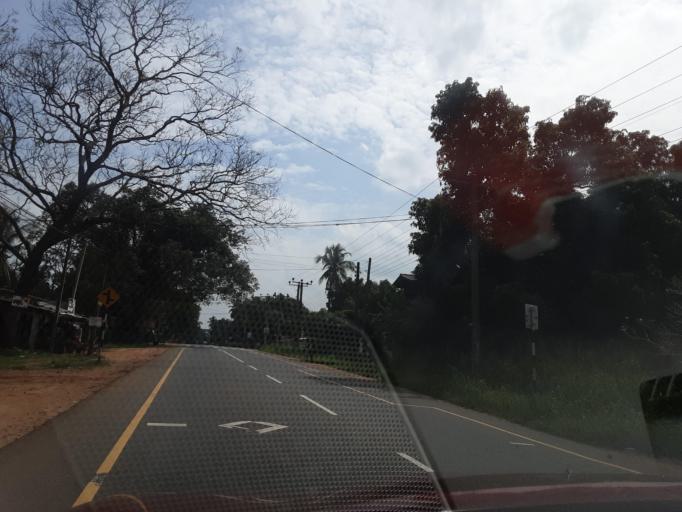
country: LK
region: Northern Province
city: Vavuniya
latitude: 8.5234
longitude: 80.5006
